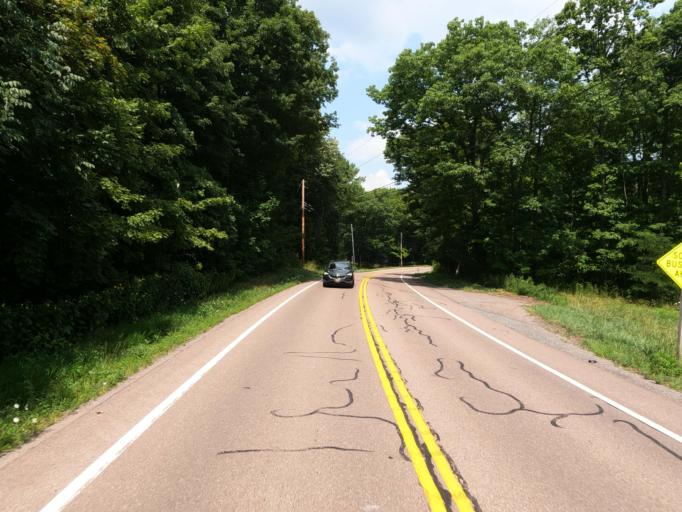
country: US
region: Maryland
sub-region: Allegany County
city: Westernport
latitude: 39.6424
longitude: -79.2015
